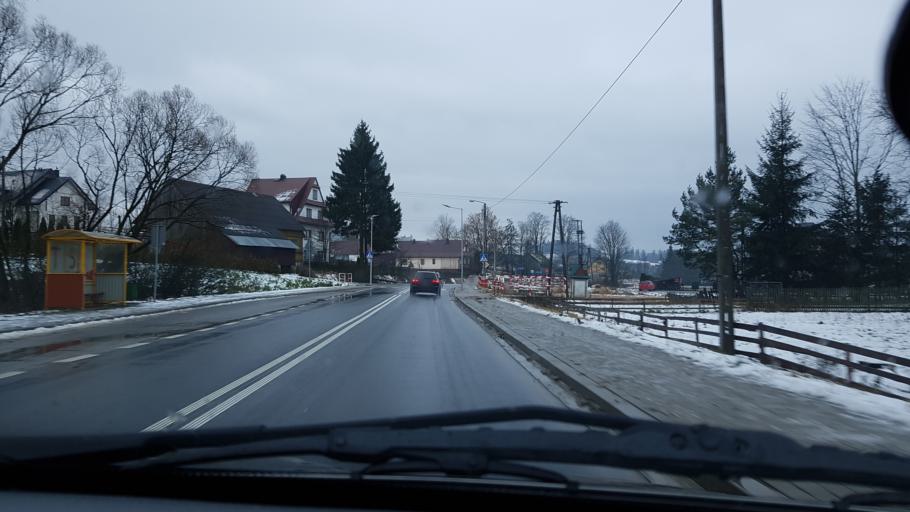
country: PL
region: Lesser Poland Voivodeship
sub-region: Powiat nowotarski
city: Sieniawa
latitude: 49.5033
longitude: 19.8878
